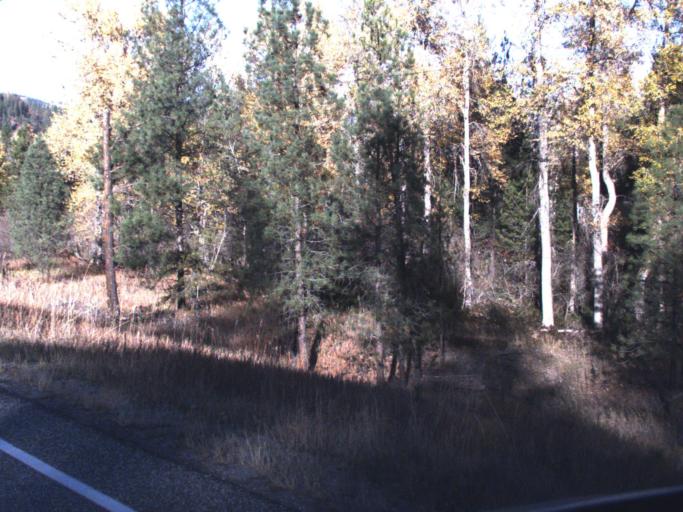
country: CA
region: British Columbia
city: Rossland
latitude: 48.9399
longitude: -117.7722
